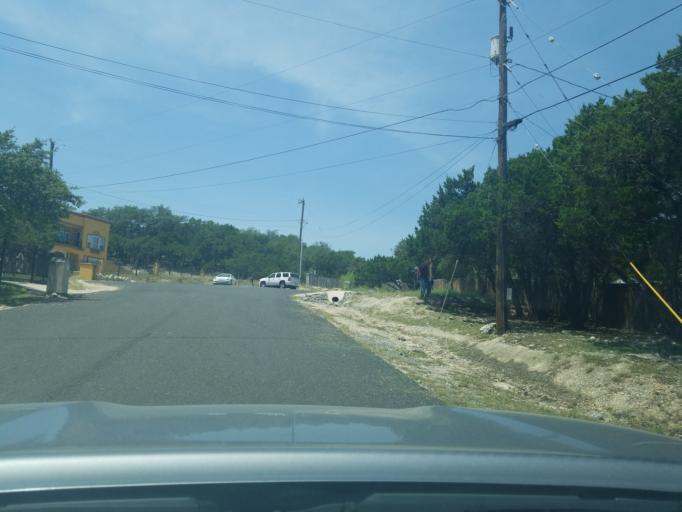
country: US
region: Texas
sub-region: Bexar County
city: Timberwood Park
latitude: 29.6722
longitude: -98.5075
